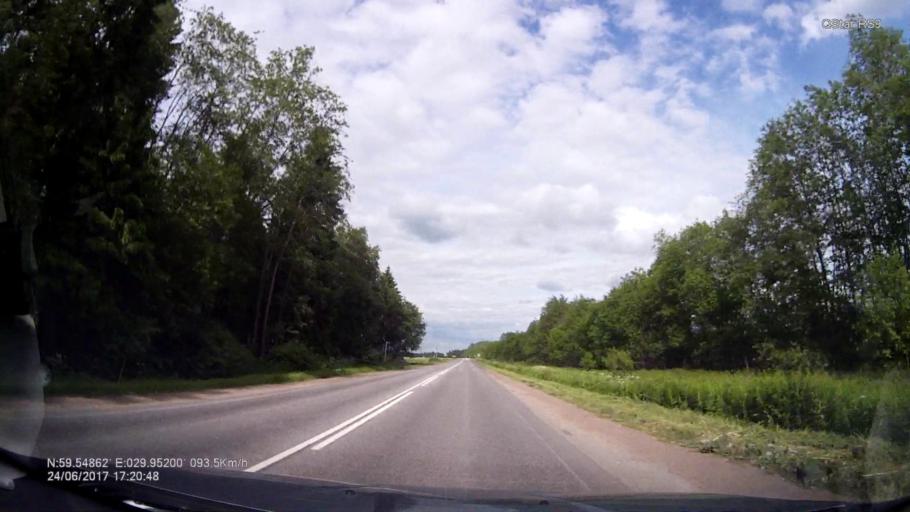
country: RU
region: Leningrad
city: Voyskovitsy
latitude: 59.5488
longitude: 29.9533
